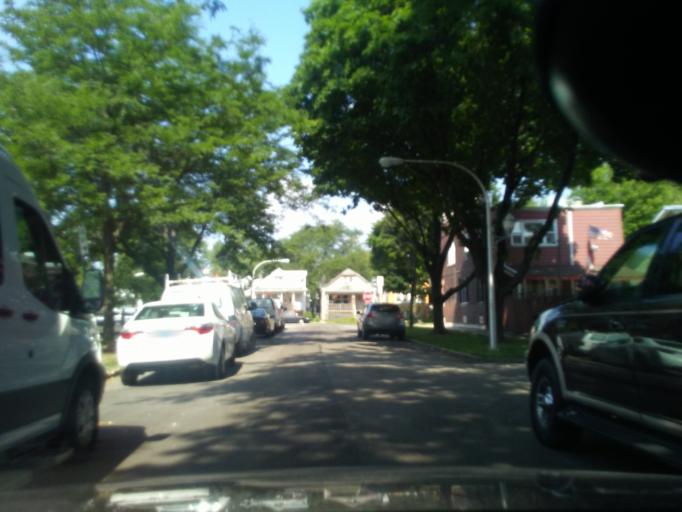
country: US
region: Illinois
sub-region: Cook County
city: Oak Park
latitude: 41.9197
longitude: -87.7478
